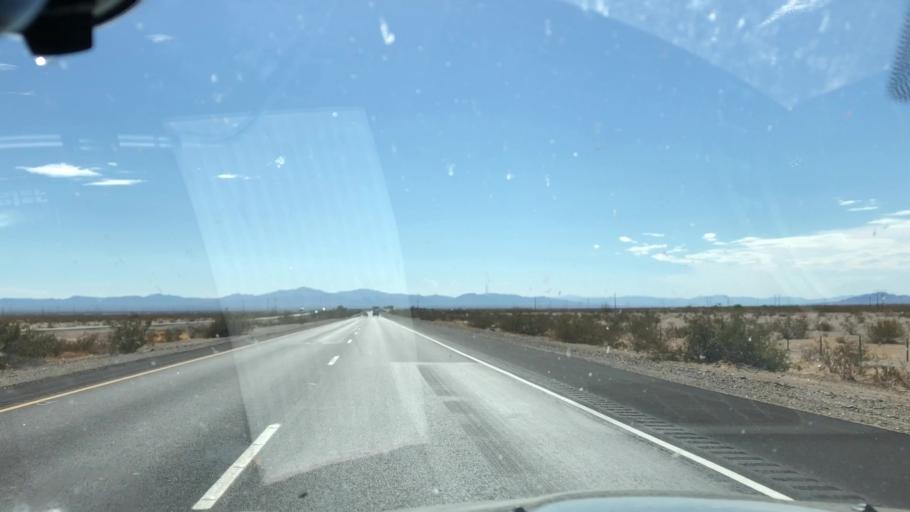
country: US
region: California
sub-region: Riverside County
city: Mesa Verde
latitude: 33.6090
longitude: -114.8745
